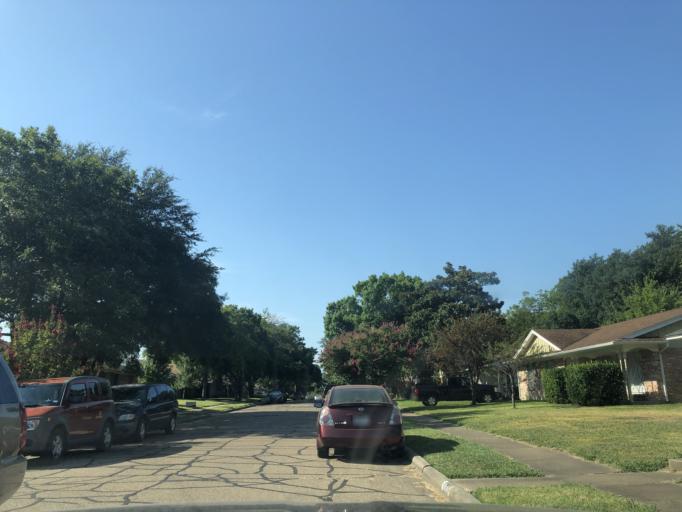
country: US
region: Texas
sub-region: Dallas County
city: Garland
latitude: 32.8673
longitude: -96.6431
